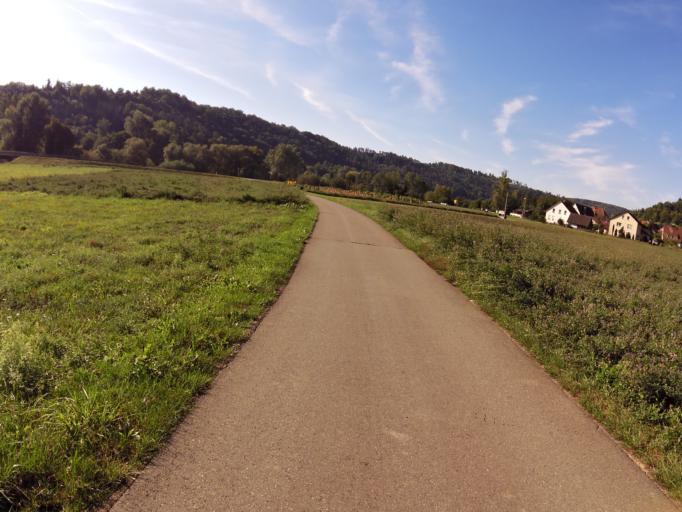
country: DE
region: Baden-Wuerttemberg
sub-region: Tuebingen Region
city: Hirrlingen
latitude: 48.4606
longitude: 8.8742
